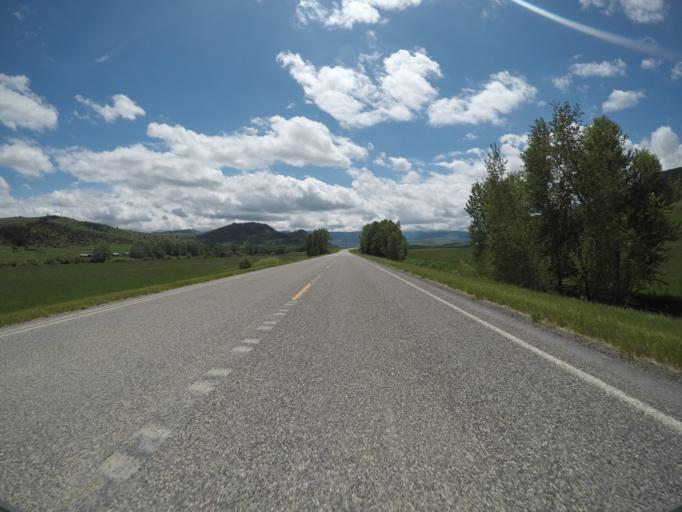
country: US
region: Montana
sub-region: Sweet Grass County
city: Big Timber
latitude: 45.6508
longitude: -110.1143
